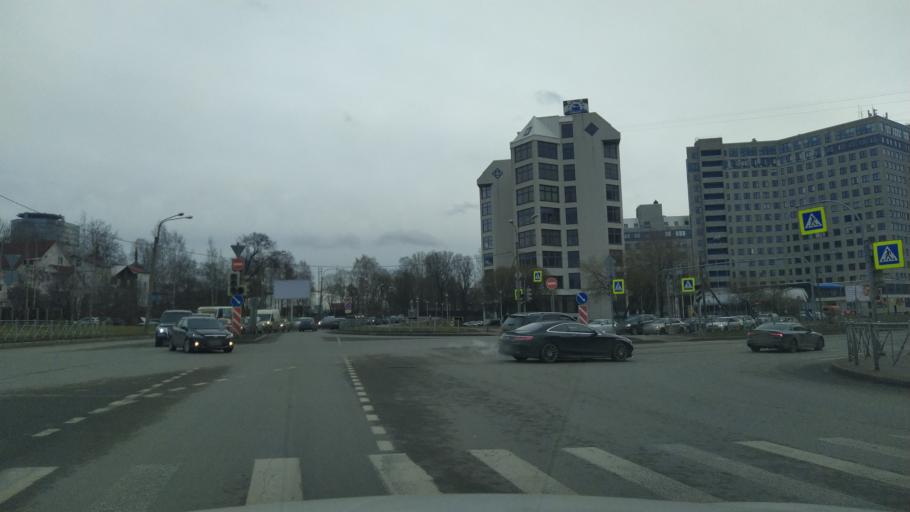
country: RU
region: St.-Petersburg
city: Kolomyagi
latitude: 60.0153
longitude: 30.2932
